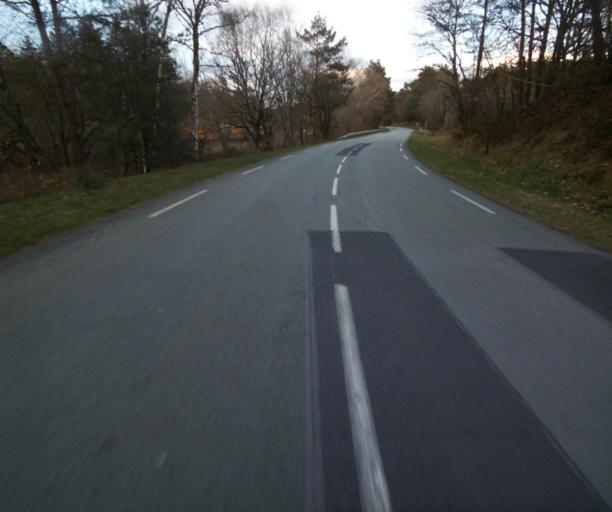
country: FR
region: Limousin
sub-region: Departement de la Correze
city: Correze
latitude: 45.2836
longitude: 1.9166
